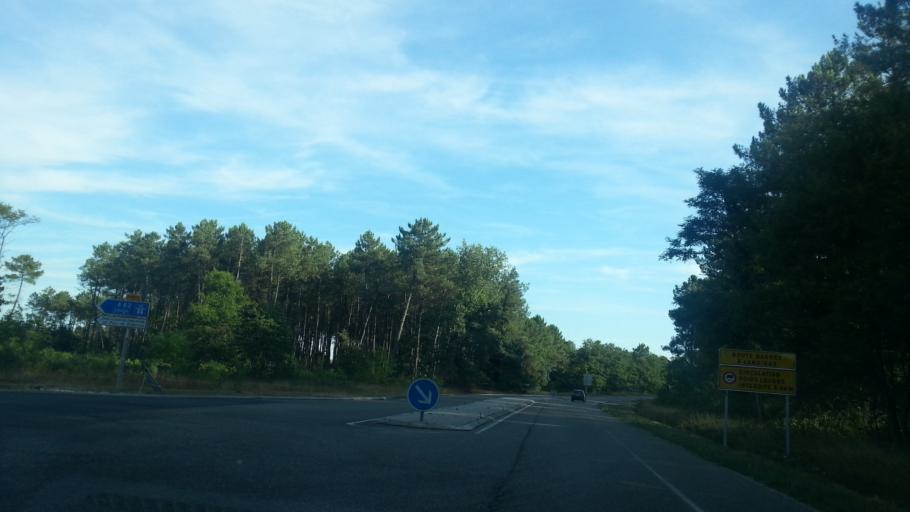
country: FR
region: Aquitaine
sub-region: Departement de la Gironde
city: Illats
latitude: 44.6122
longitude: -0.3723
